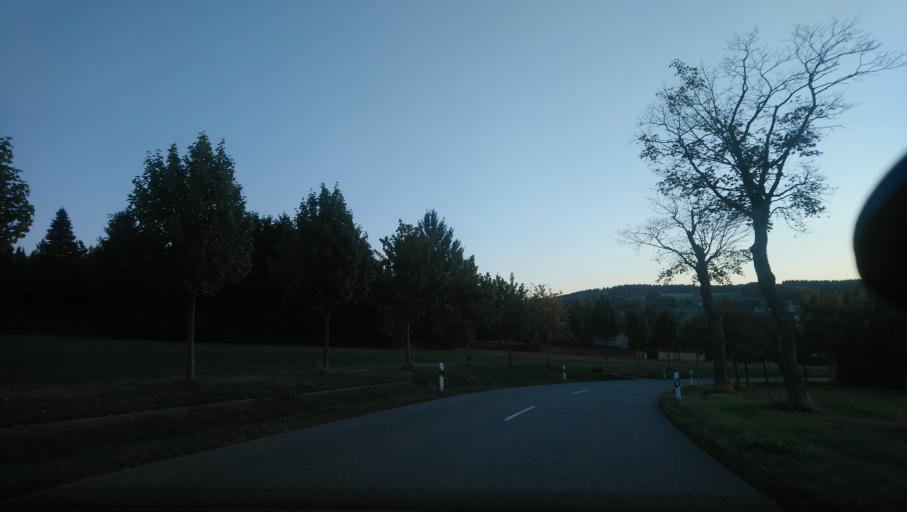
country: DE
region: Saxony
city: Geyer
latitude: 50.6324
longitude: 12.9201
